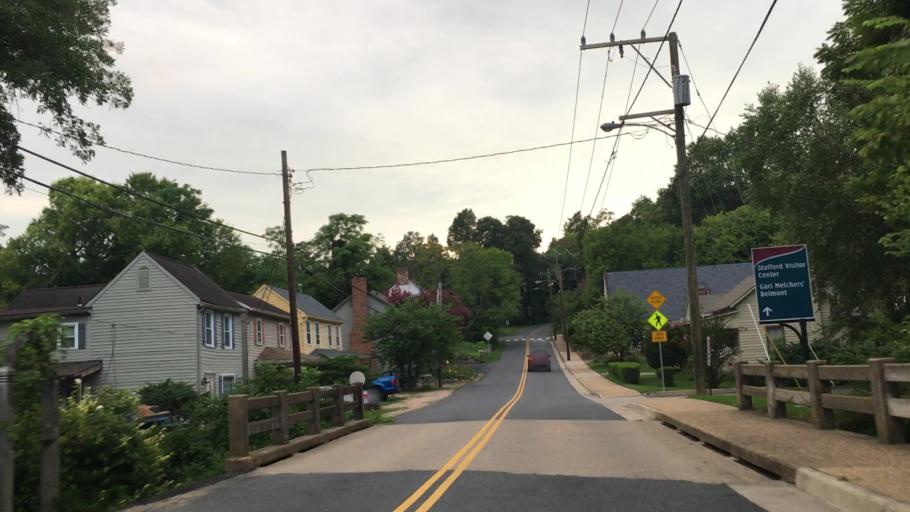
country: US
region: Virginia
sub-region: Stafford County
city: Falmouth
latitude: 38.3231
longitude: -77.4702
